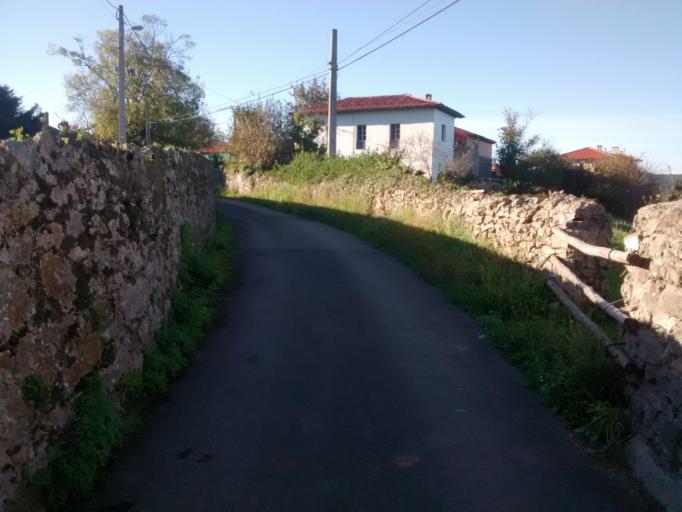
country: ES
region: Asturias
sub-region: Province of Asturias
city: Colunga
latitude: 43.4692
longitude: -5.2348
